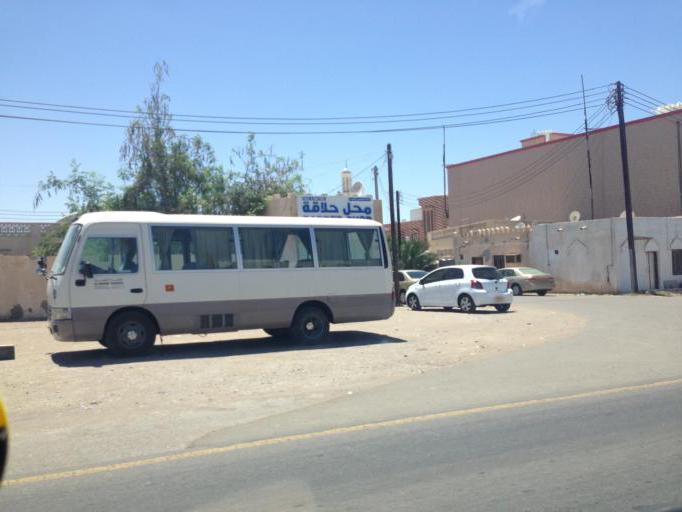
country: OM
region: Muhafazat Masqat
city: As Sib al Jadidah
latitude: 23.6618
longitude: 58.2106
